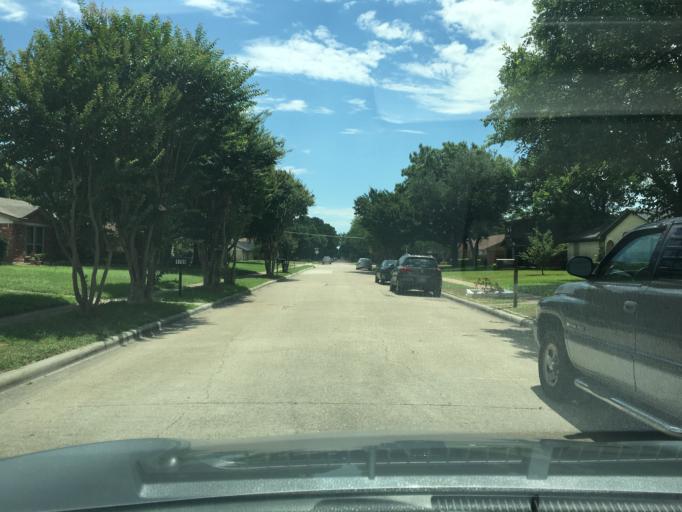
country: US
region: Texas
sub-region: Dallas County
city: Richardson
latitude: 32.9336
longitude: -96.6921
